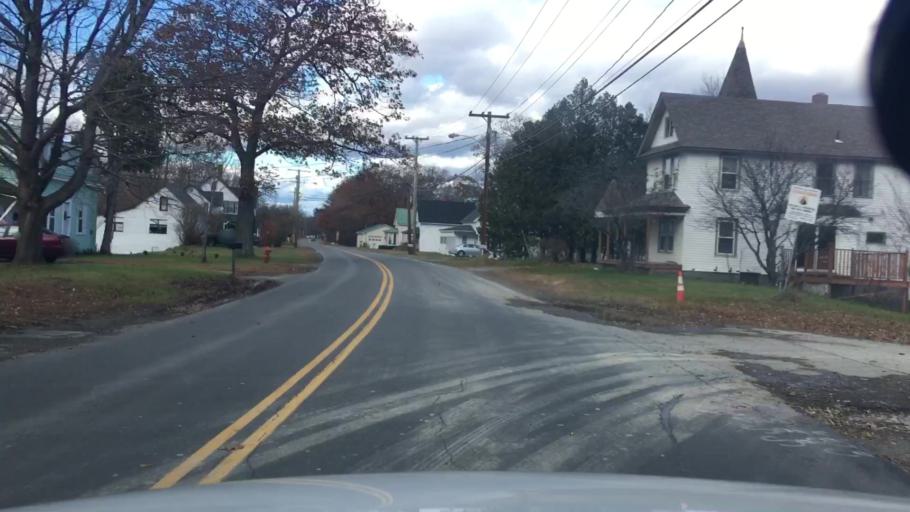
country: US
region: Maine
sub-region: Somerset County
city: Saint Albans
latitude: 44.8776
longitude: -69.4486
